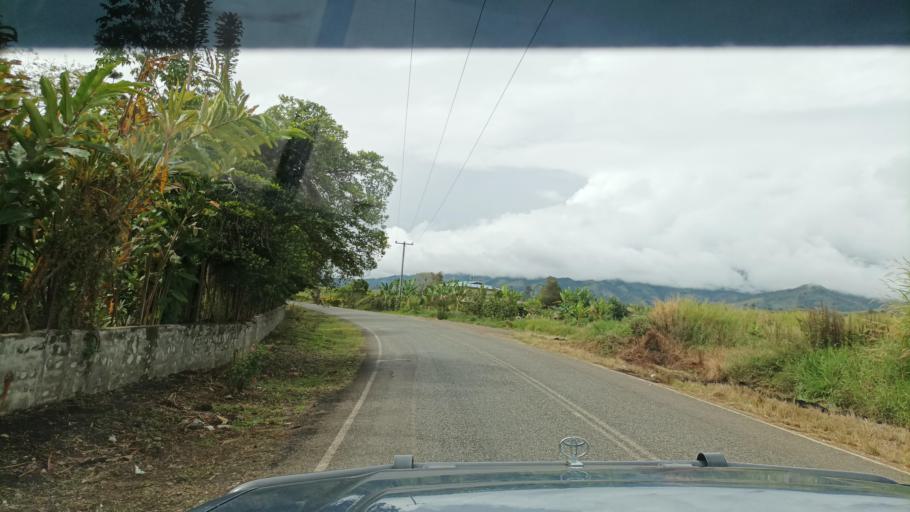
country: PG
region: Jiwaka
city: Minj
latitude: -5.8970
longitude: 144.6827
